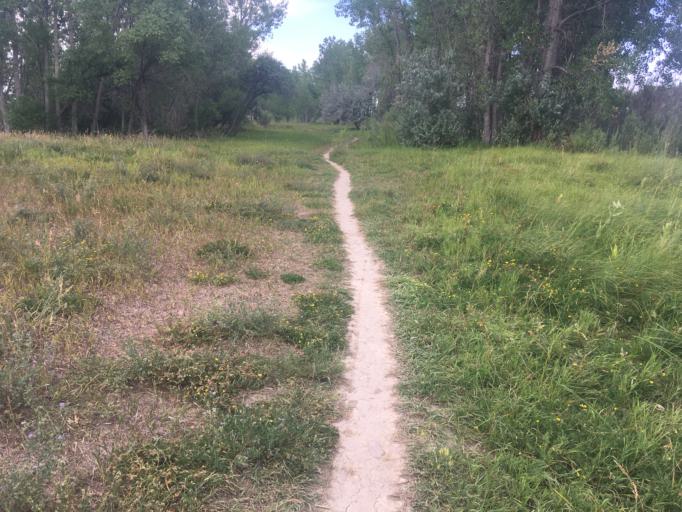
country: US
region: Colorado
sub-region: Boulder County
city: Superior
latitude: 39.9728
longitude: -105.2259
